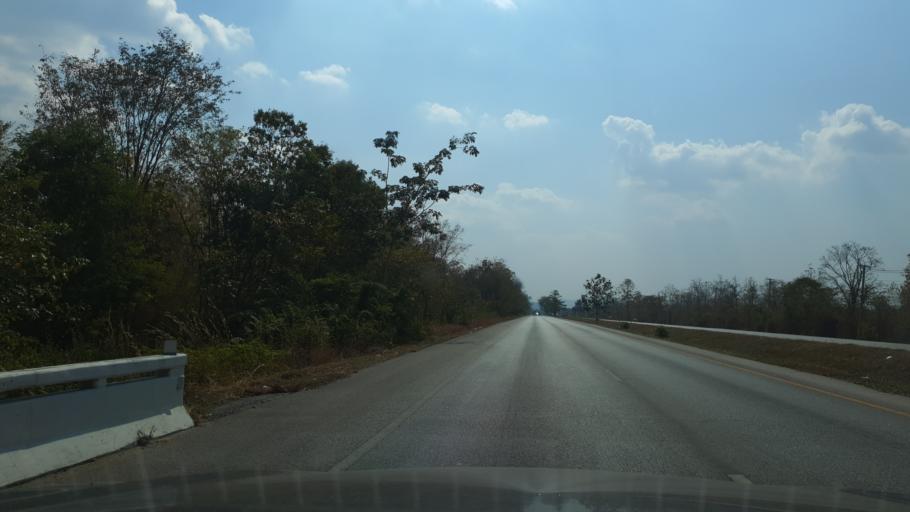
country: TH
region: Lampang
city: Mae Phrik
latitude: 17.4373
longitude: 99.1588
